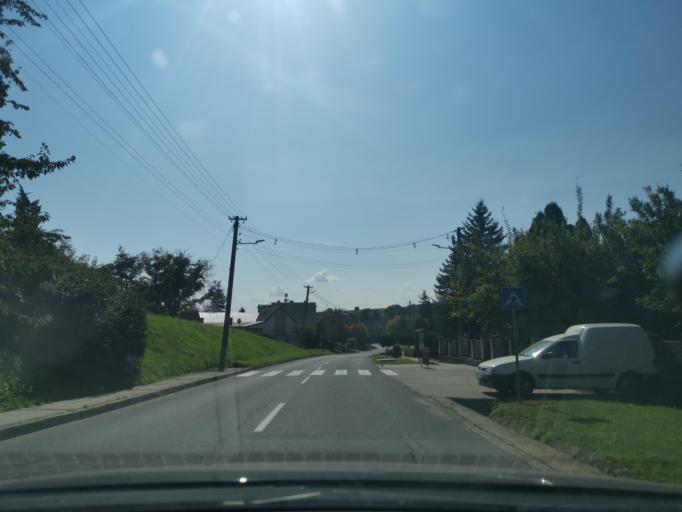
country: SK
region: Trnavsky
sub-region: Okres Senica
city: Senica
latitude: 48.7076
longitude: 17.2839
